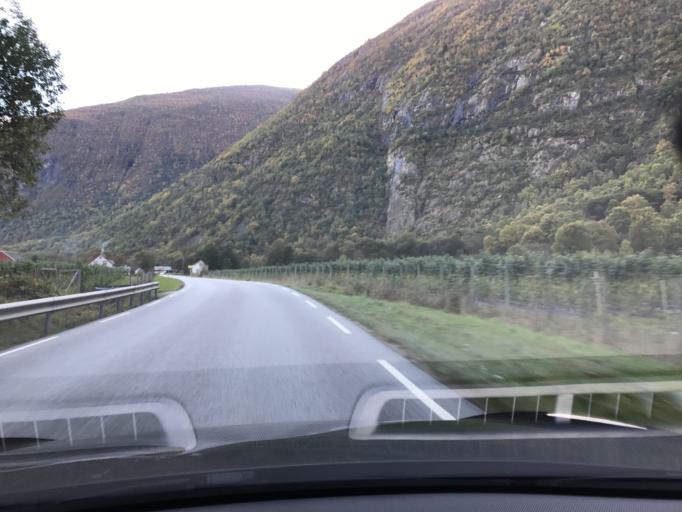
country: NO
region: Sogn og Fjordane
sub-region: Laerdal
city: Laerdalsoyri
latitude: 61.0740
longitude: 7.5007
